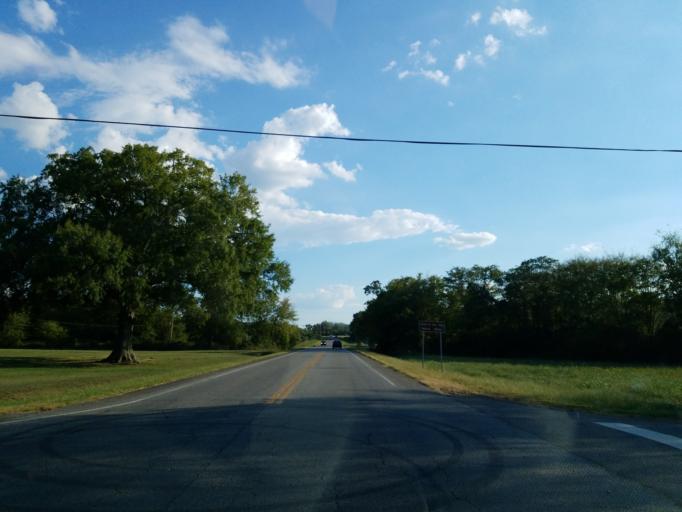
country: US
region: Georgia
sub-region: Murray County
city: Chatsworth
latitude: 34.8860
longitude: -84.7502
